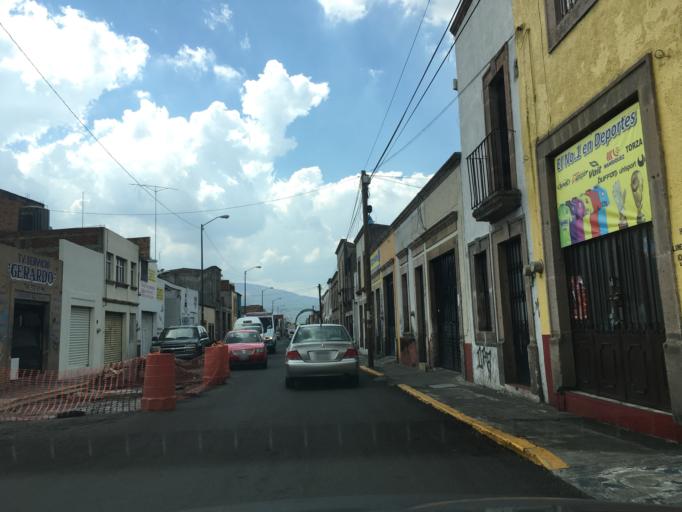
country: MX
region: Michoacan
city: Morelia
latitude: 19.6993
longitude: -101.2018
